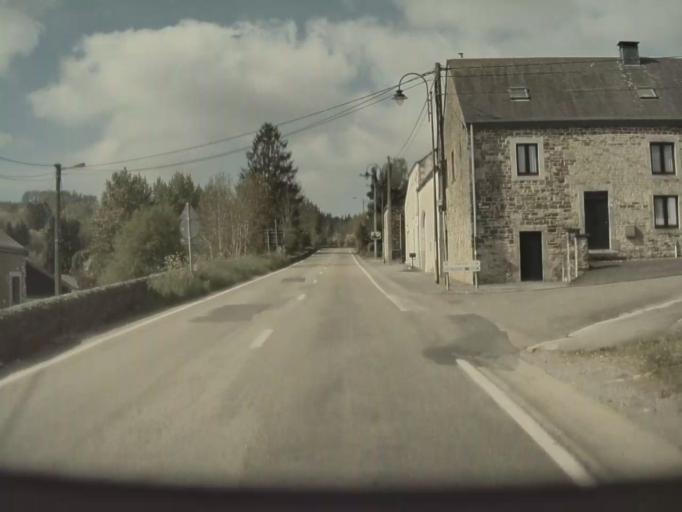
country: BE
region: Wallonia
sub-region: Province du Luxembourg
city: Tellin
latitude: 50.0803
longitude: 5.2163
